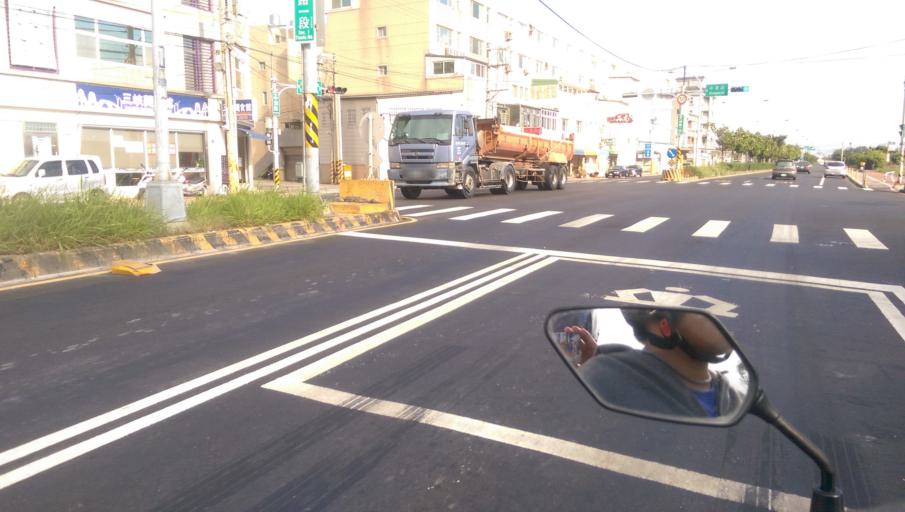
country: TW
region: Taiwan
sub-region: Hsinchu
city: Hsinchu
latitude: 24.8389
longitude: 120.9348
